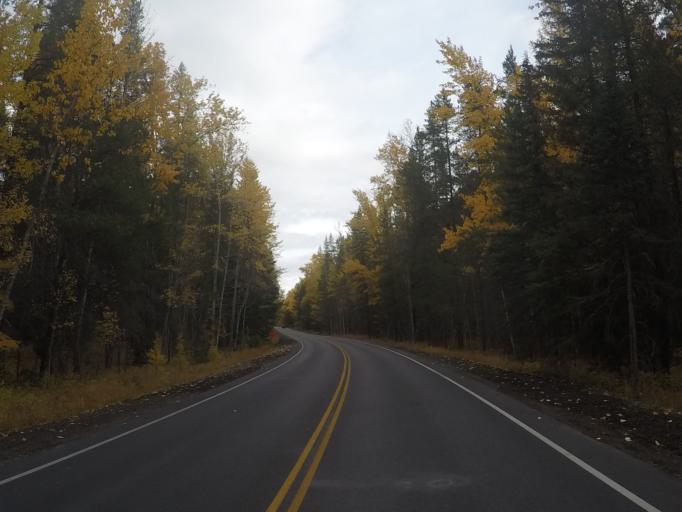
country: US
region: Montana
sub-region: Flathead County
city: Columbia Falls
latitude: 48.5227
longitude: -113.9801
